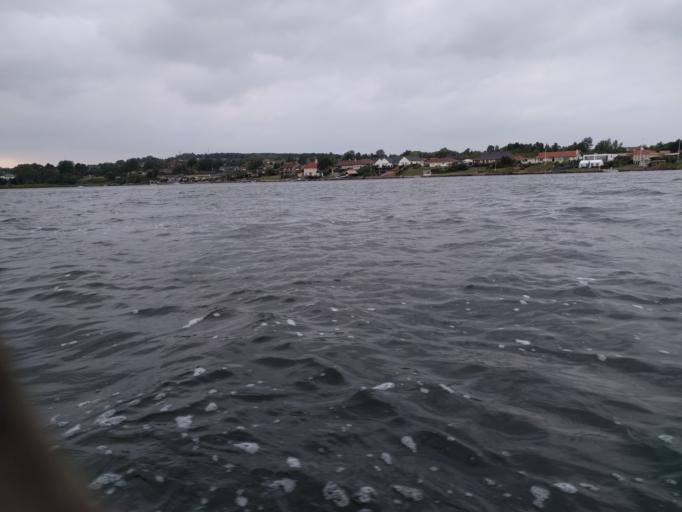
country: DK
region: South Denmark
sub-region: Kerteminde Kommune
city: Munkebo
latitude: 55.4597
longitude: 10.5893
